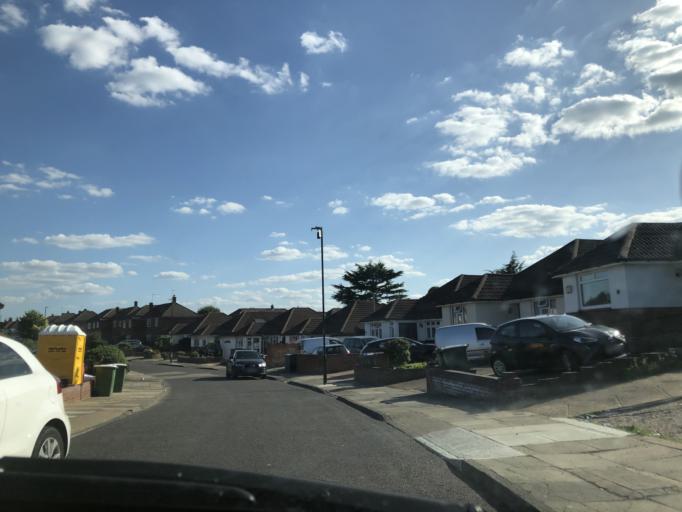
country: GB
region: England
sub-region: Greater London
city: Bexley
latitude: 51.4392
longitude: 0.1662
